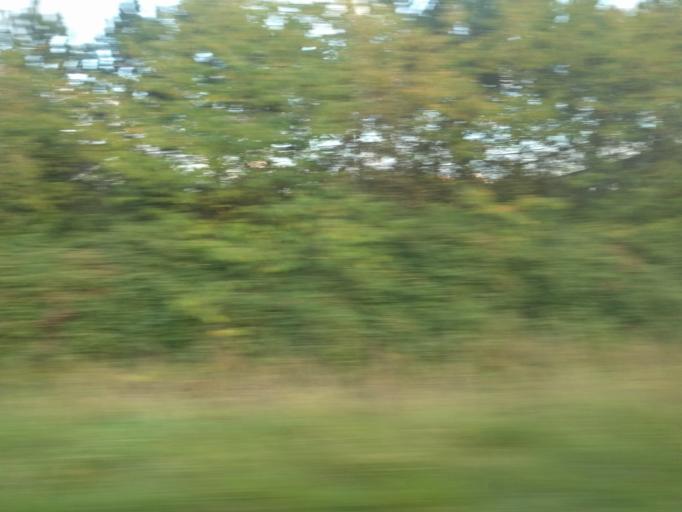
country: DK
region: South Denmark
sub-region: Kerteminde Kommune
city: Langeskov
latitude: 55.3583
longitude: 10.6021
